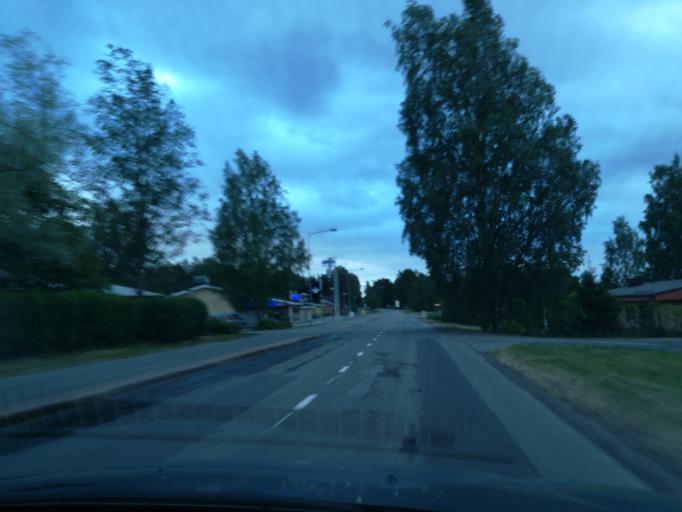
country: FI
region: Southern Savonia
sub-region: Mikkeli
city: Ristiina
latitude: 61.5118
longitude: 27.2452
